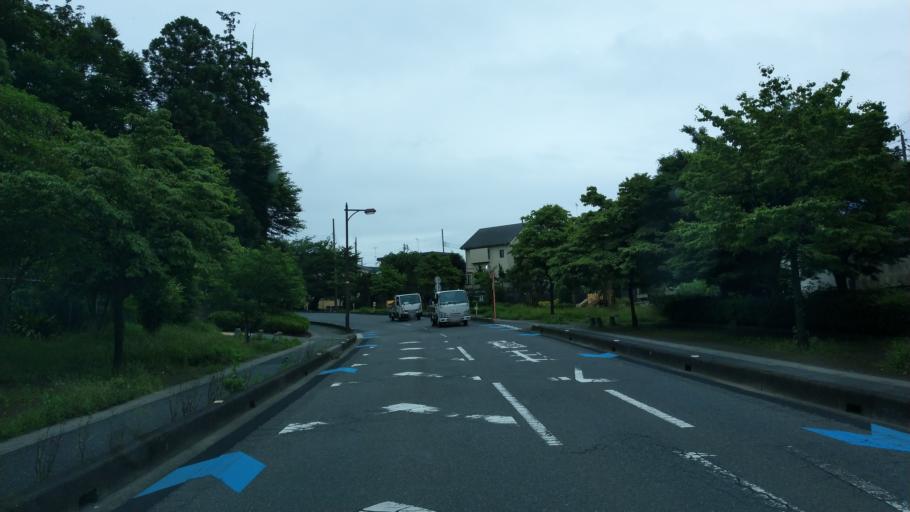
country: JP
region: Saitama
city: Saitama
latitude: 35.9312
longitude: 139.6435
